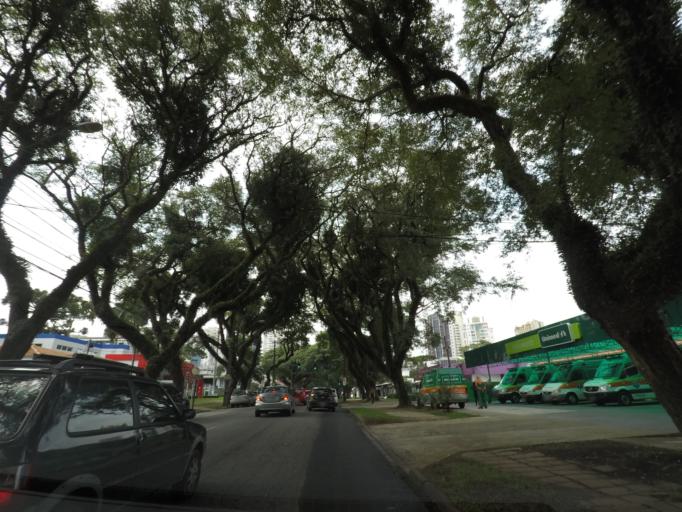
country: BR
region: Parana
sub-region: Curitiba
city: Curitiba
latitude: -25.4529
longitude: -49.2928
